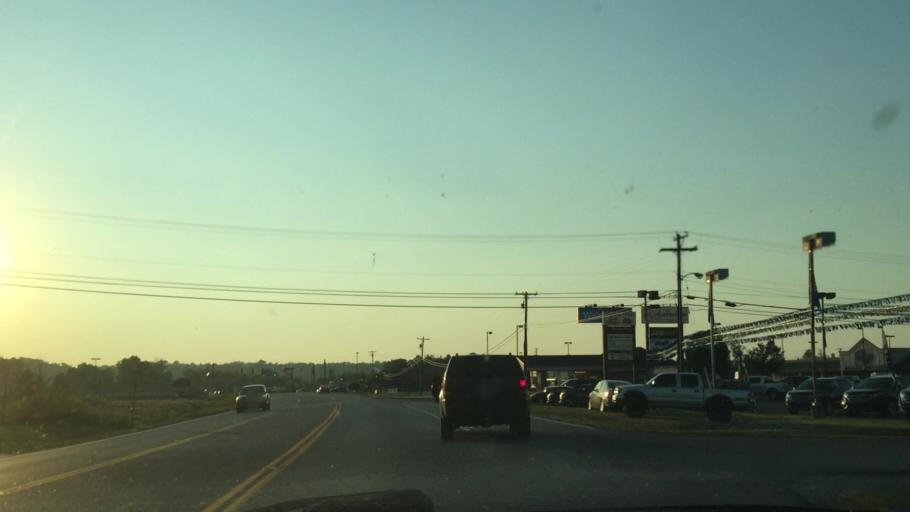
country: US
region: Kentucky
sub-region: Carroll County
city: Carrollton
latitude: 38.6557
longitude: -85.1305
